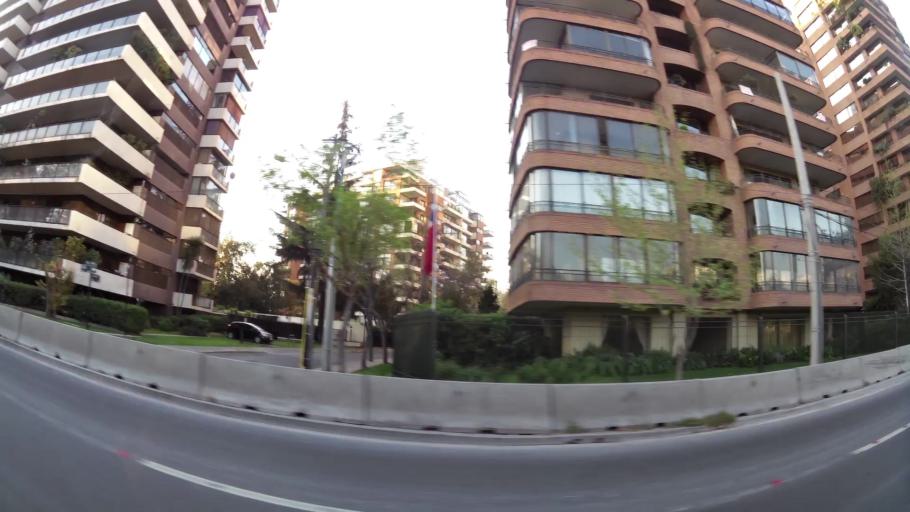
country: CL
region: Santiago Metropolitan
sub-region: Provincia de Santiago
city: Villa Presidente Frei, Nunoa, Santiago, Chile
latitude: -33.4047
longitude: -70.5894
